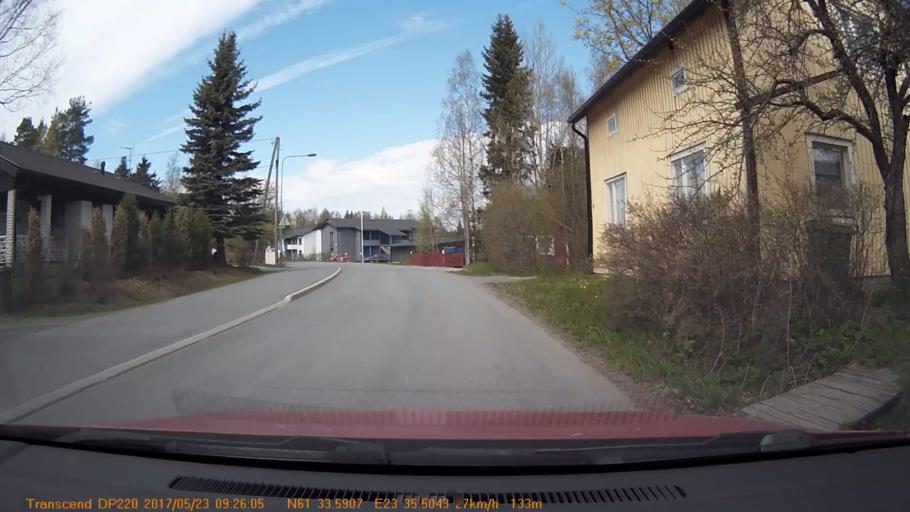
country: FI
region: Pirkanmaa
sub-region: Tampere
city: Yloejaervi
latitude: 61.5599
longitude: 23.5918
